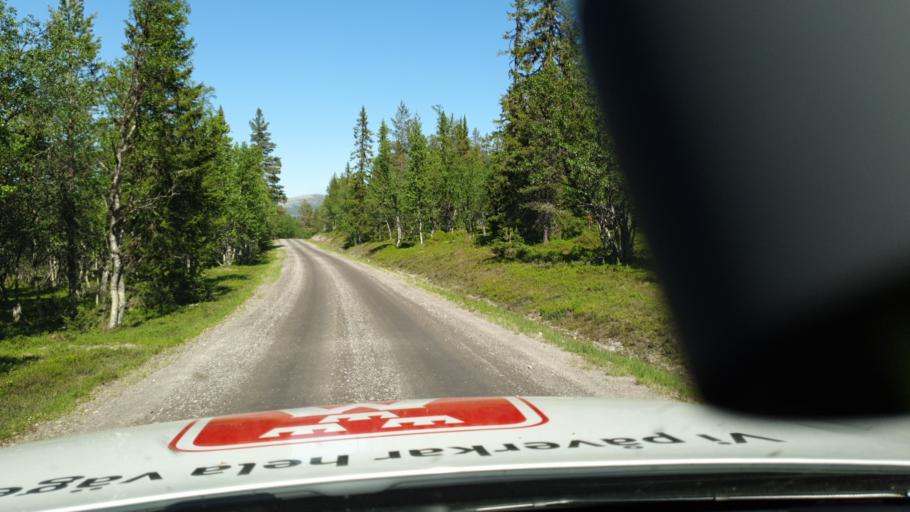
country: NO
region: Hedmark
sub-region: Engerdal
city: Engerdal
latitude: 62.1421
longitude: 12.9462
